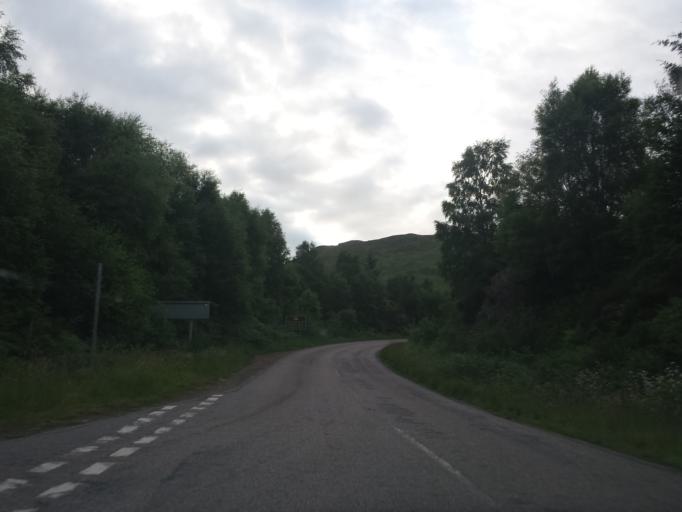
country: GB
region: Scotland
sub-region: Highland
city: Portree
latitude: 57.2859
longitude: -5.5814
